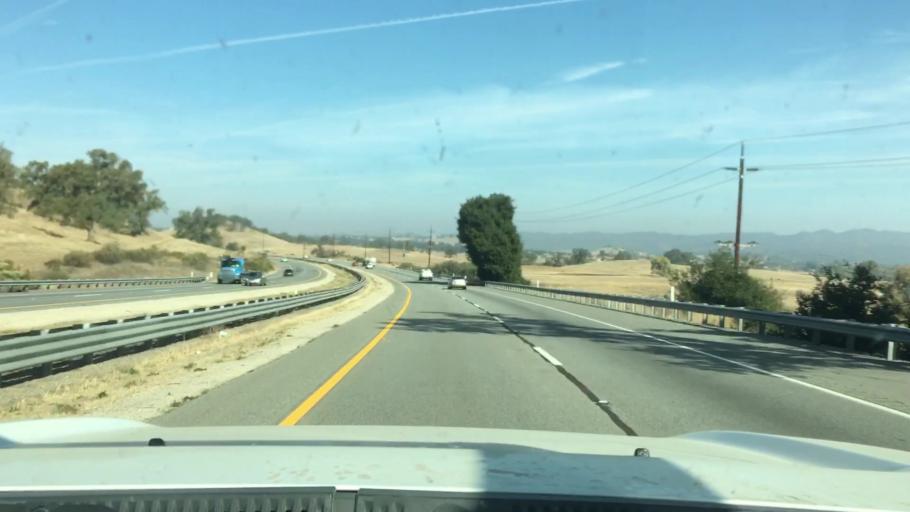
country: US
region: California
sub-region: San Luis Obispo County
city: Santa Margarita
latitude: 35.3970
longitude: -120.6226
